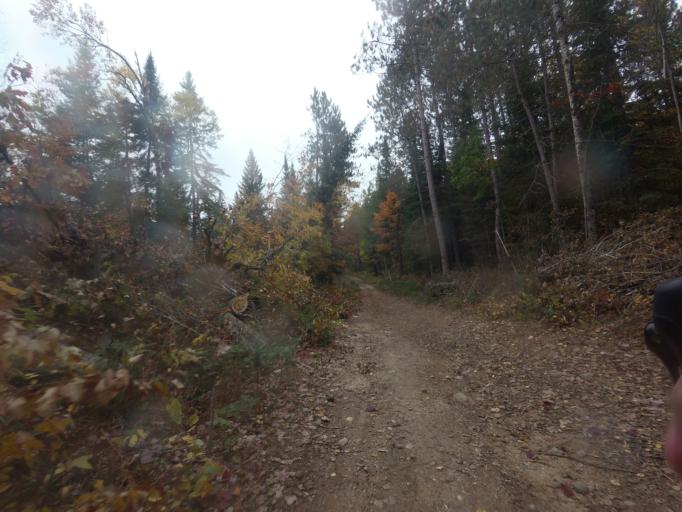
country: CA
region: Ontario
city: Petawawa
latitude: 45.7712
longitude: -77.3724
